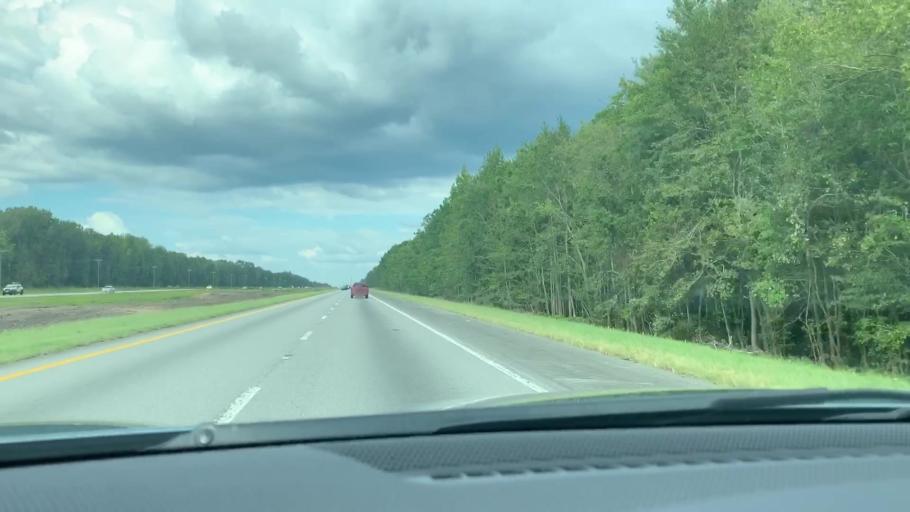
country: US
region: South Carolina
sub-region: Jasper County
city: Ridgeland
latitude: 32.5413
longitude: -80.9526
